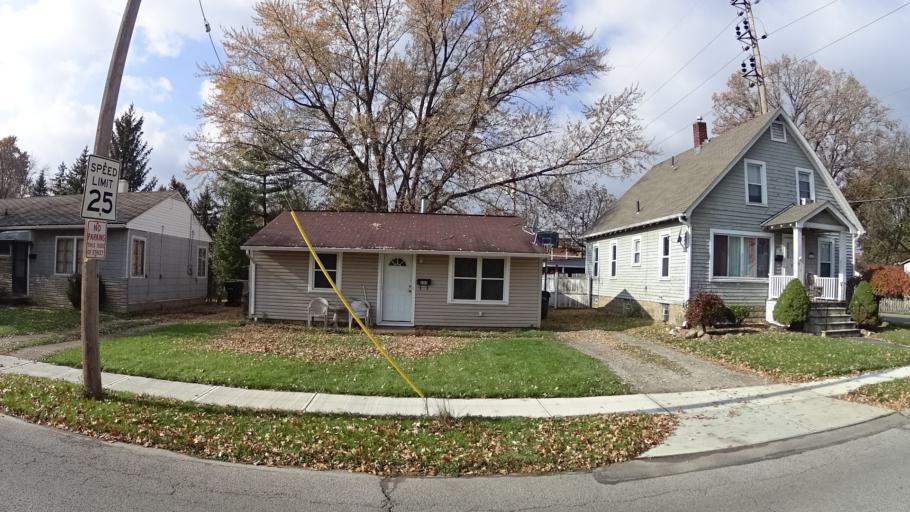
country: US
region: Ohio
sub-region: Lorain County
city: Elyria
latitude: 41.3685
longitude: -82.0861
